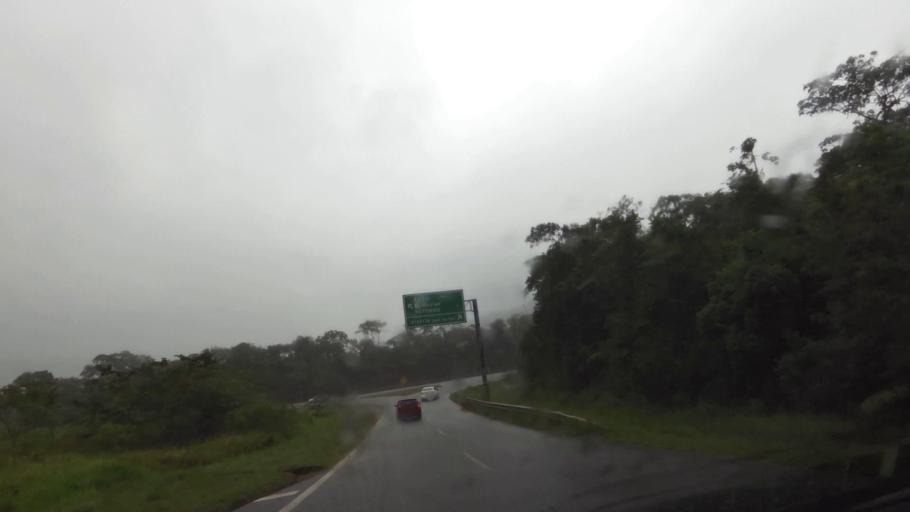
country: BR
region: Espirito Santo
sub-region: Guarapari
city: Guarapari
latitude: -20.6328
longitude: -40.5181
